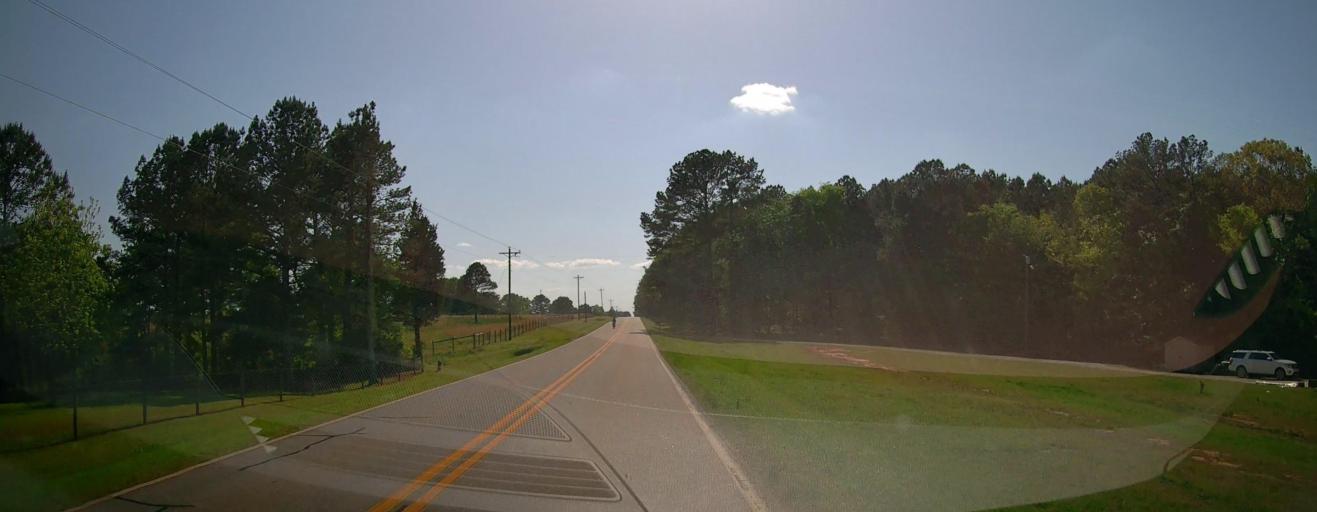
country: US
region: Georgia
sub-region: Morgan County
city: Madison
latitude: 33.6628
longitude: -83.4860
